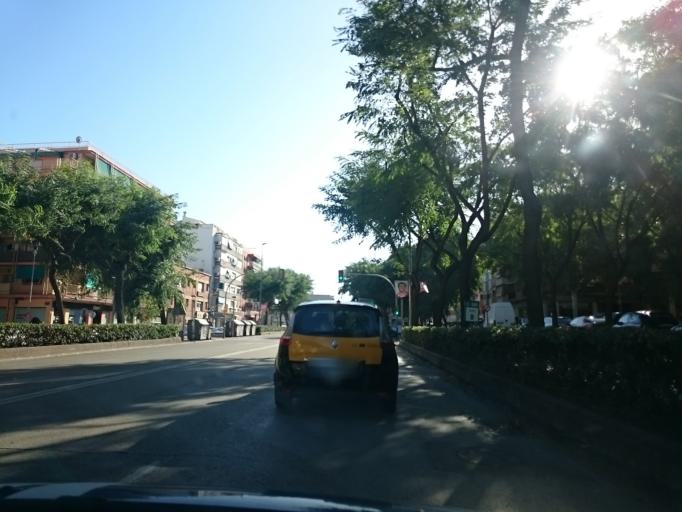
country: ES
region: Catalonia
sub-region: Provincia de Barcelona
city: Viladecans
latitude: 41.3193
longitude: 2.0250
